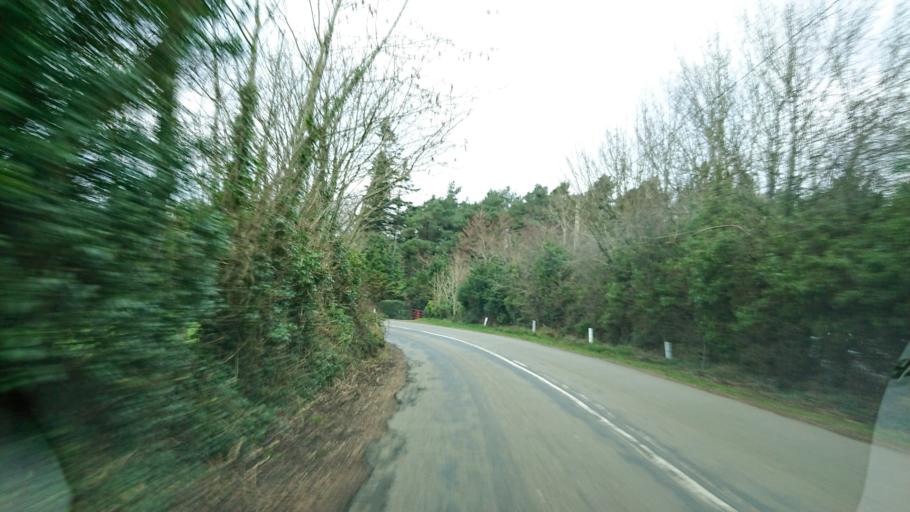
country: IE
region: Munster
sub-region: South Tipperary
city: Cluain Meala
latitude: 52.3232
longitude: -7.5753
